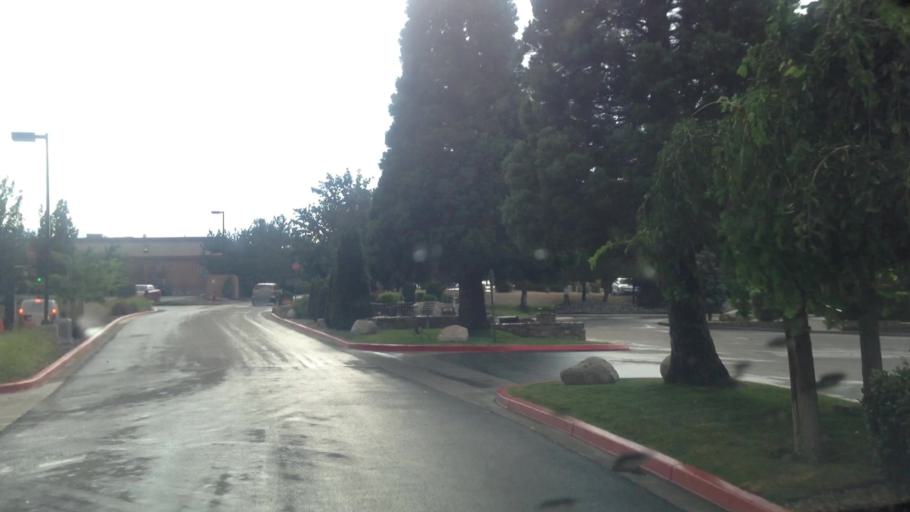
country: US
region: Nevada
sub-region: Washoe County
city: Reno
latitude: 39.4777
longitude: -119.7915
